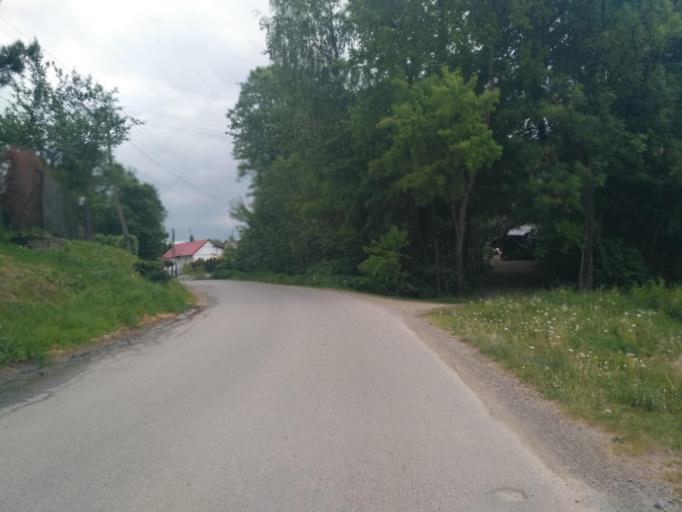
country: PL
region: Subcarpathian Voivodeship
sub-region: Powiat krosnienski
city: Jedlicze
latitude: 49.6873
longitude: 21.6449
